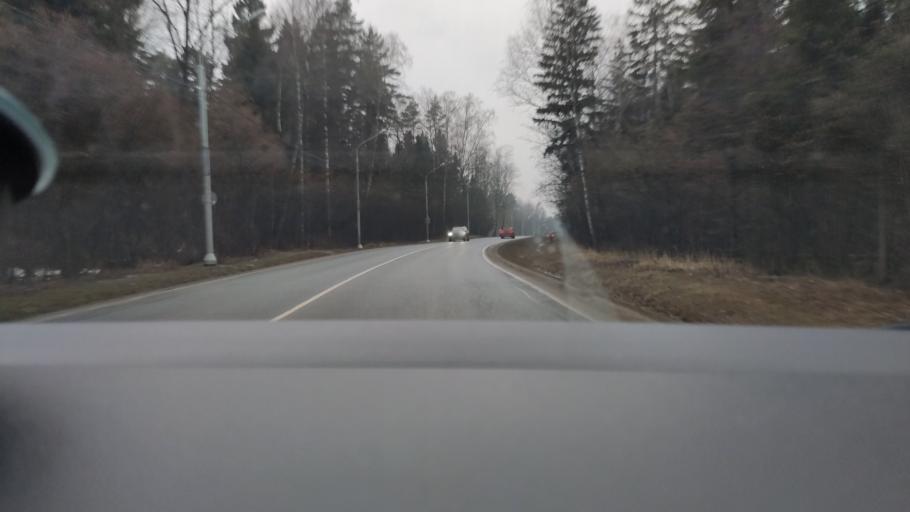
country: RU
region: Moskovskaya
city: Gorki Vtoryye
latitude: 55.6991
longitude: 37.1203
